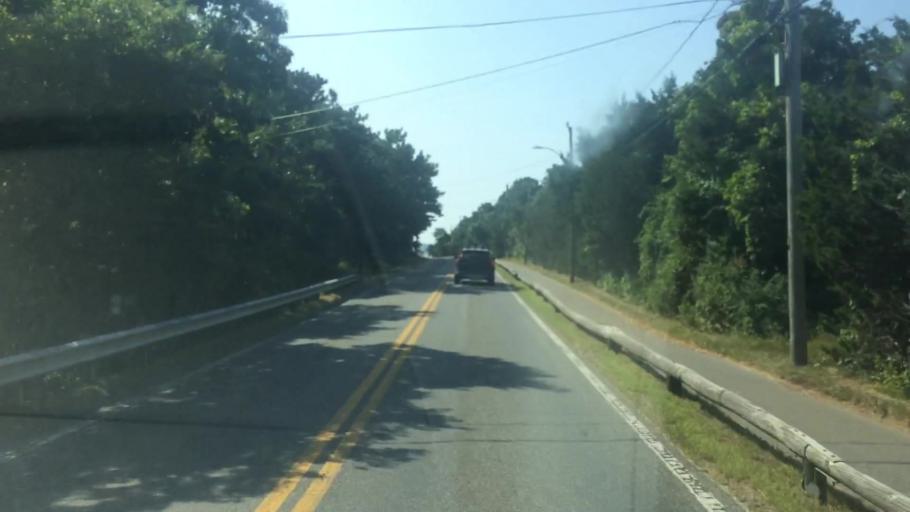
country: US
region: Massachusetts
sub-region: Dukes County
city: Oak Bluffs
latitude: 41.4366
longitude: -70.5572
